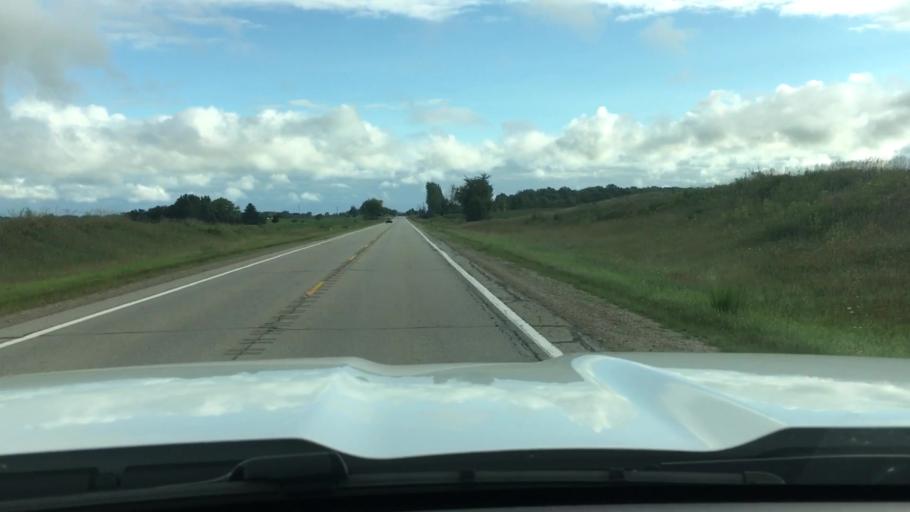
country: US
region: Michigan
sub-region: Tuscola County
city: Cass City
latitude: 43.5719
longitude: -83.2988
